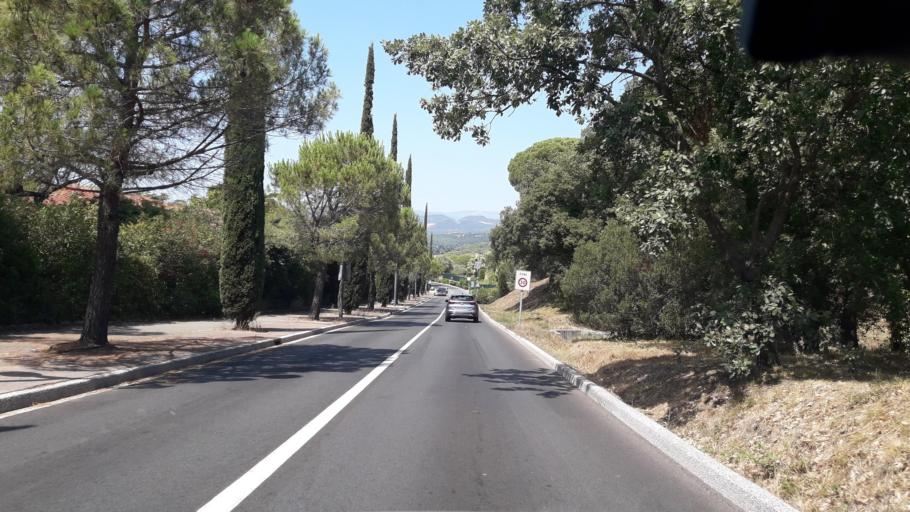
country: FR
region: Provence-Alpes-Cote d'Azur
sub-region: Departement du Var
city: Frejus
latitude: 43.4483
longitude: 6.7486
